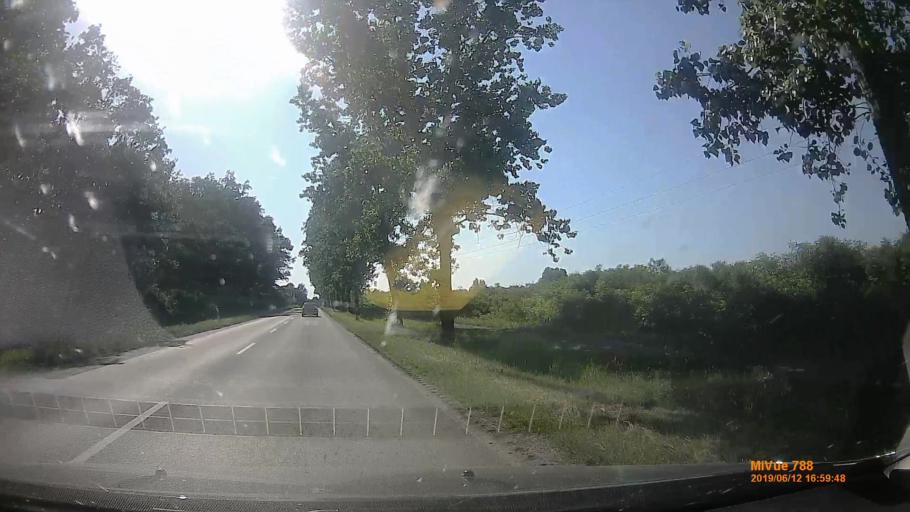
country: HU
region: Csongrad
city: Deszk
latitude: 46.2195
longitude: 20.2596
